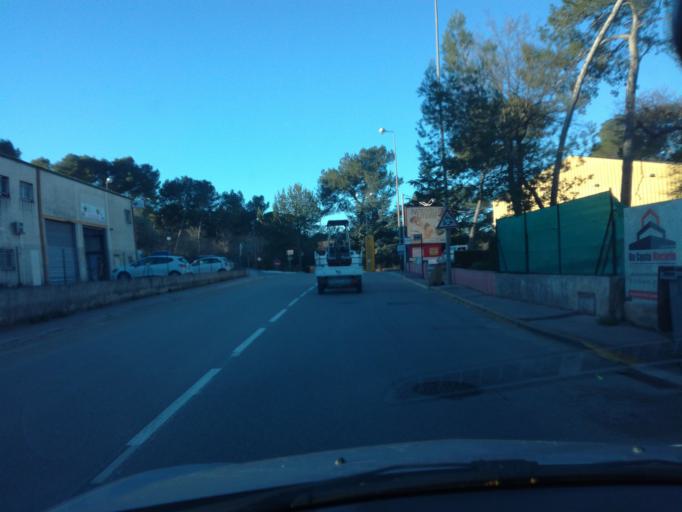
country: FR
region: Provence-Alpes-Cote d'Azur
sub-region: Departement des Alpes-Maritimes
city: La Roquette-sur-Siagne
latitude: 43.5992
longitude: 6.9691
